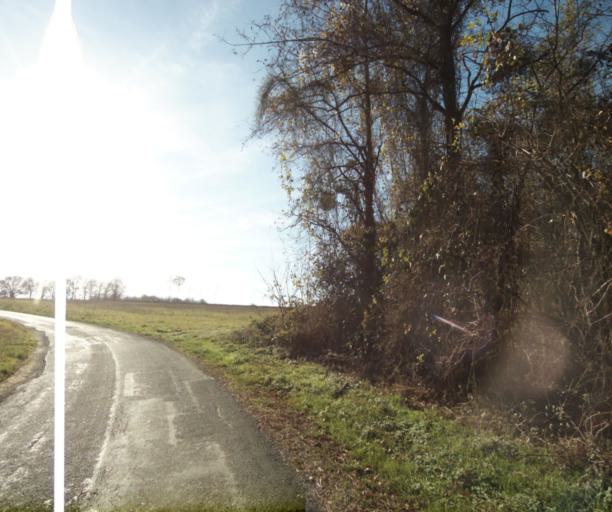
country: FR
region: Poitou-Charentes
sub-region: Departement de la Charente-Maritime
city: Ecoyeux
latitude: 45.7599
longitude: -0.5102
